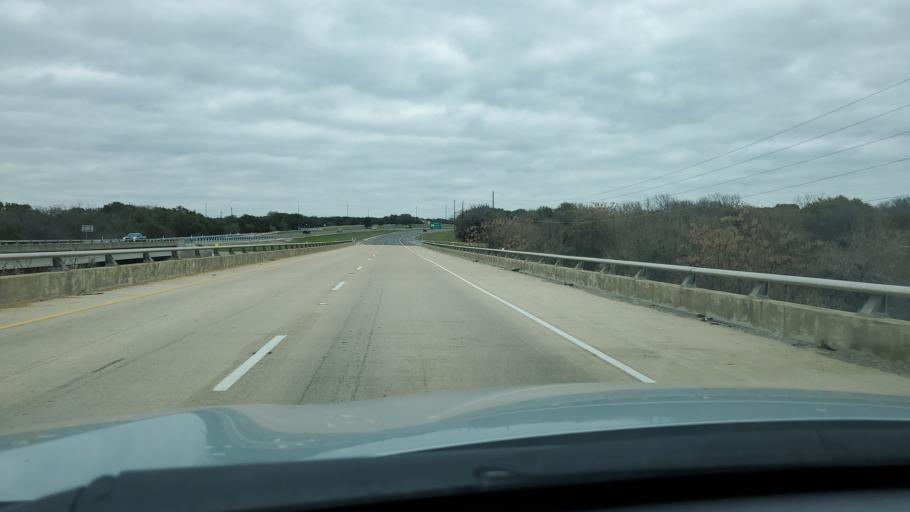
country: US
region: Texas
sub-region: Williamson County
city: Florence
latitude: 30.9720
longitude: -97.7784
